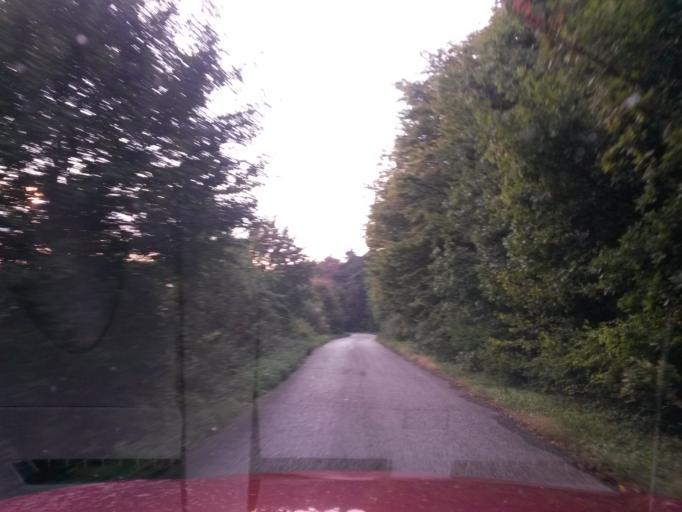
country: SK
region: Kosicky
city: Kosice
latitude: 48.7656
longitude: 21.4557
